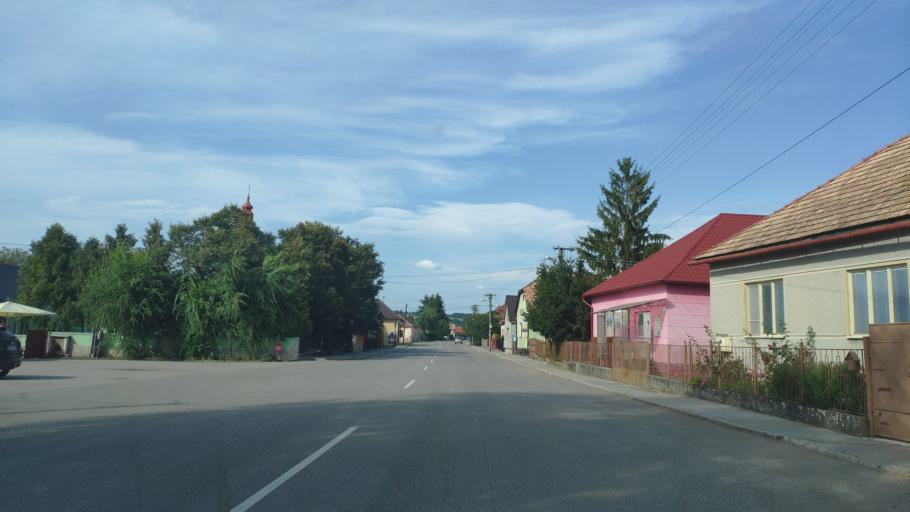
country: HU
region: Borsod-Abauj-Zemplen
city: Putnok
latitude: 48.4727
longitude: 20.3510
